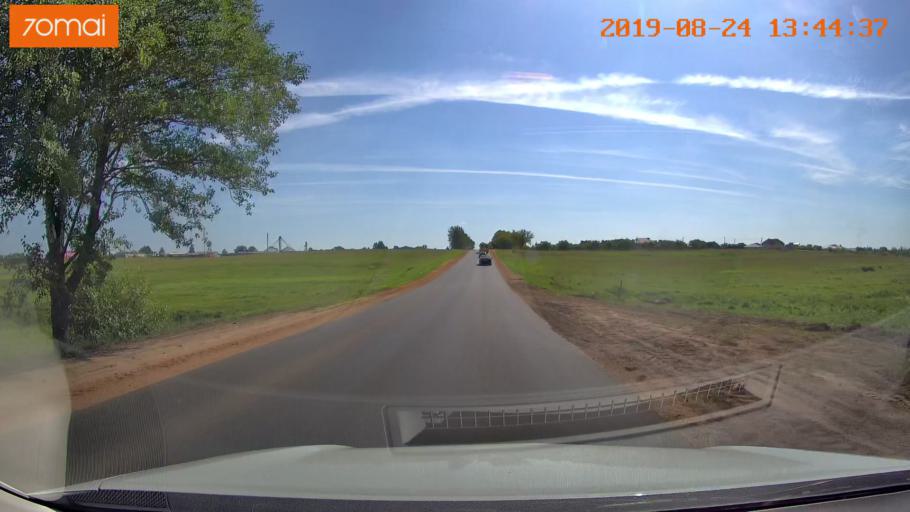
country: BY
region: Minsk
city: Samakhvalavichy
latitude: 53.6868
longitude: 27.5256
